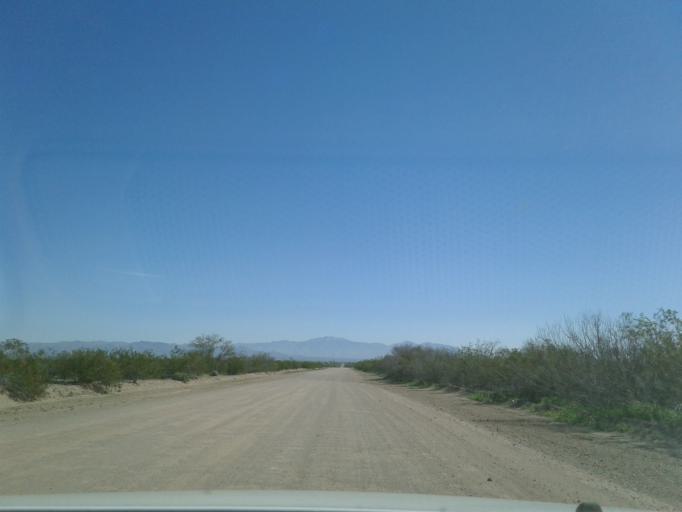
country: US
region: Arizona
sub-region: Pima County
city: Avra Valley
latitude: 32.4293
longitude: -111.3583
